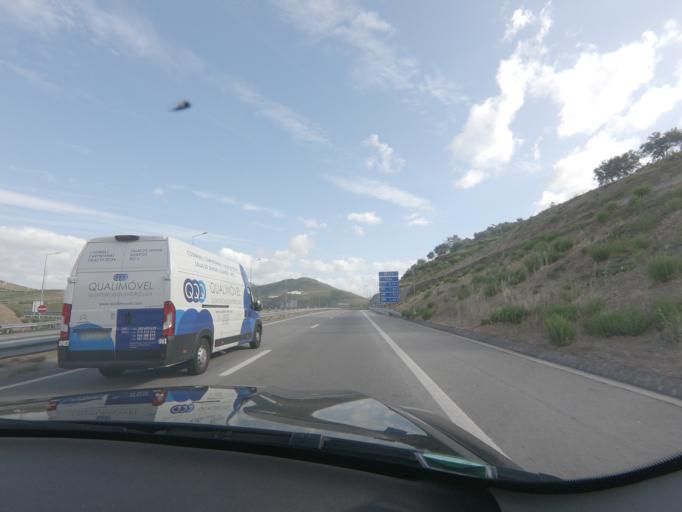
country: PT
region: Vila Real
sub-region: Peso da Regua
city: Peso da Regua
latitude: 41.1669
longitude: -7.7712
